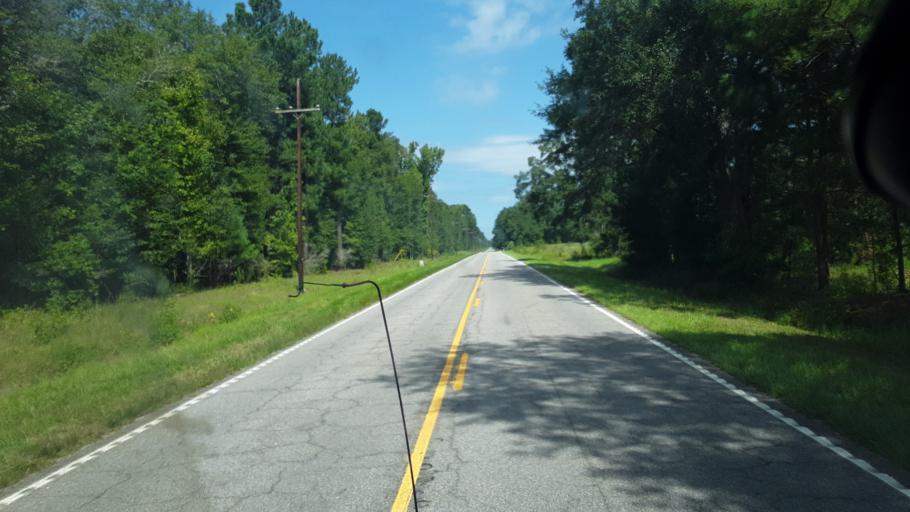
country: US
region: South Carolina
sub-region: Bamberg County
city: Bamberg
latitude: 33.2378
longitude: -81.0315
